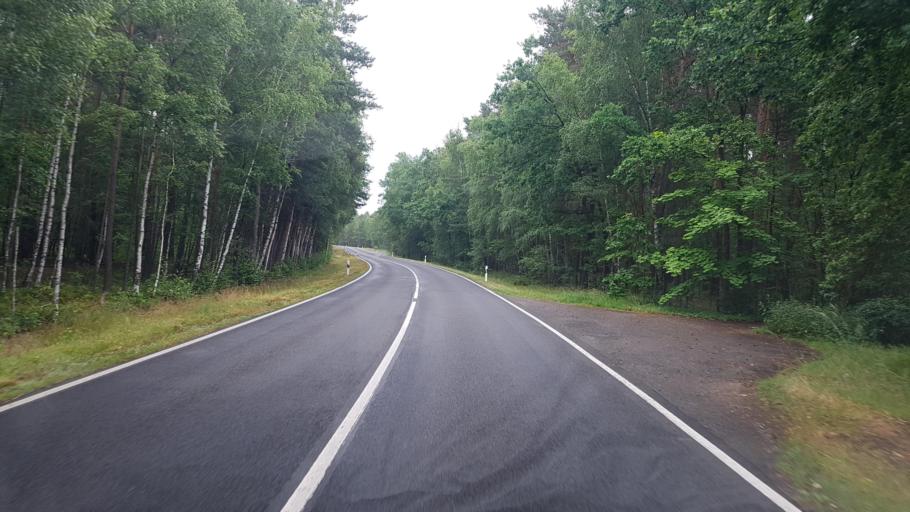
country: DE
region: Brandenburg
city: Kroppen
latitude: 51.3900
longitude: 13.8255
